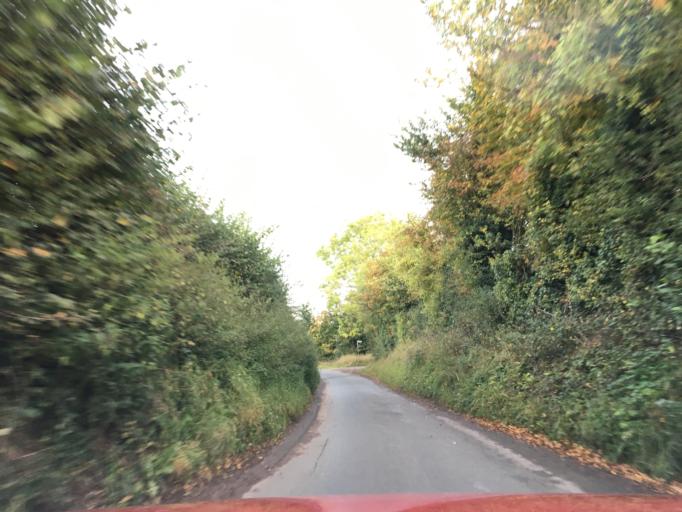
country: GB
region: England
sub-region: South Gloucestershire
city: Alveston
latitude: 51.6110
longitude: -2.5598
